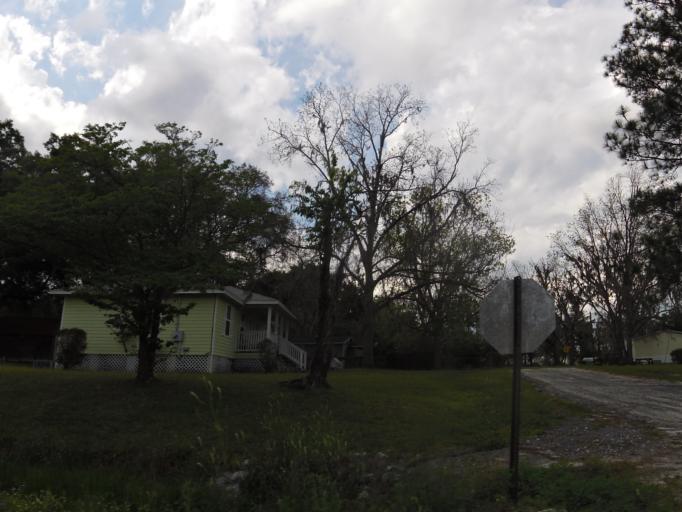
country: US
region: Georgia
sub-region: Charlton County
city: Folkston
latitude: 30.8259
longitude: -82.0386
